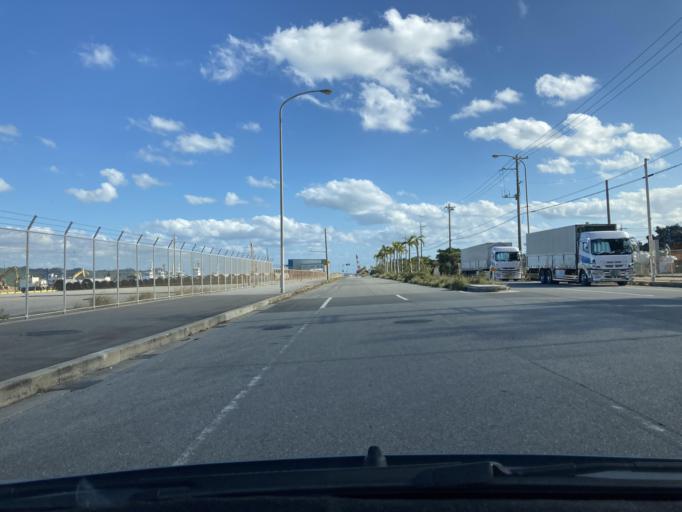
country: JP
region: Okinawa
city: Katsuren-haebaru
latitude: 26.3313
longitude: 127.8539
